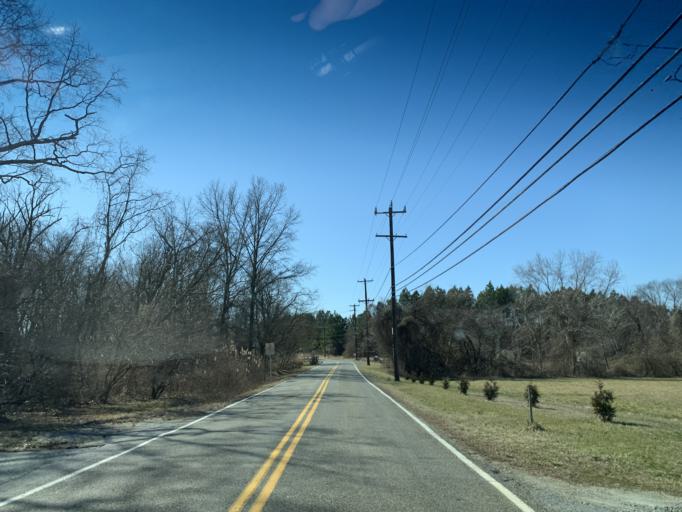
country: US
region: Maryland
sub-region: Cecil County
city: Elkton
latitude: 39.5164
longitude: -75.8250
